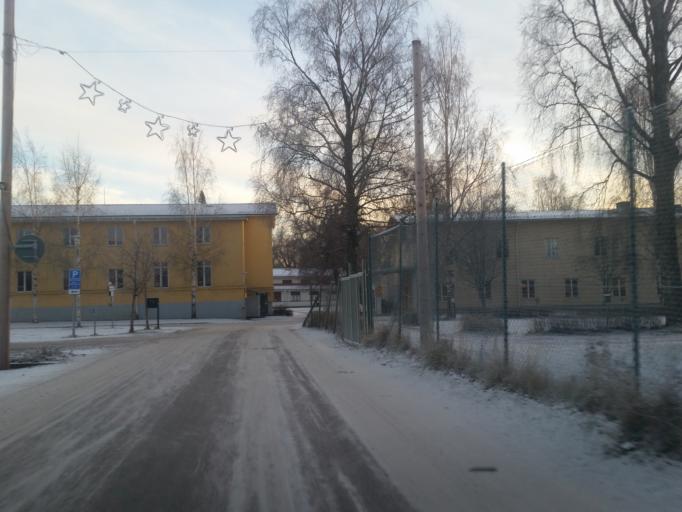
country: SE
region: Dalarna
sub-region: Leksand Municipality
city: Leksand
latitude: 60.7335
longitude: 14.9871
